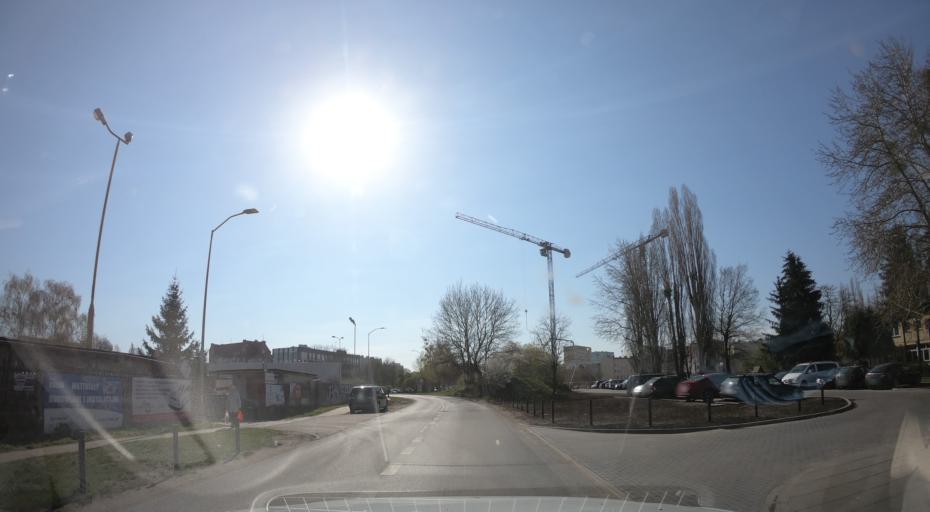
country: PL
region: West Pomeranian Voivodeship
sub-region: Szczecin
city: Szczecin
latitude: 53.4416
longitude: 14.5715
